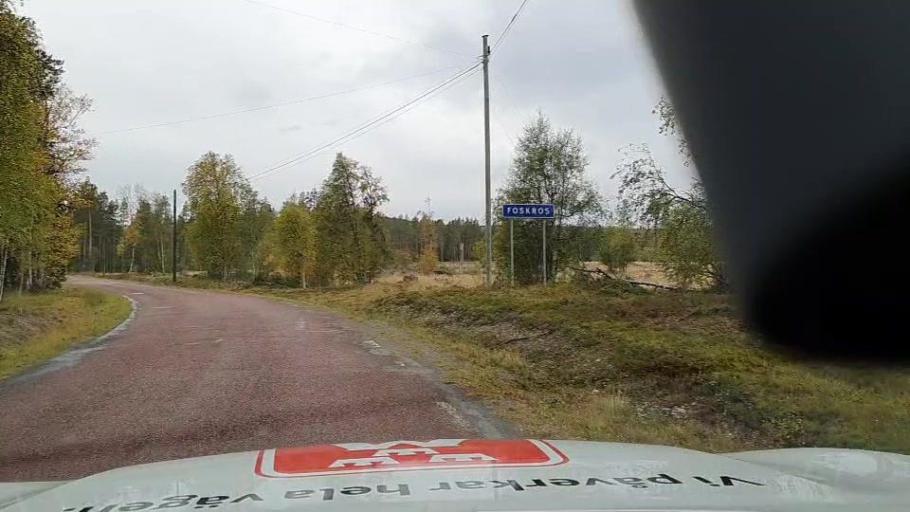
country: NO
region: Hedmark
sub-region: Engerdal
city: Engerdal
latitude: 62.0151
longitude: 12.6714
